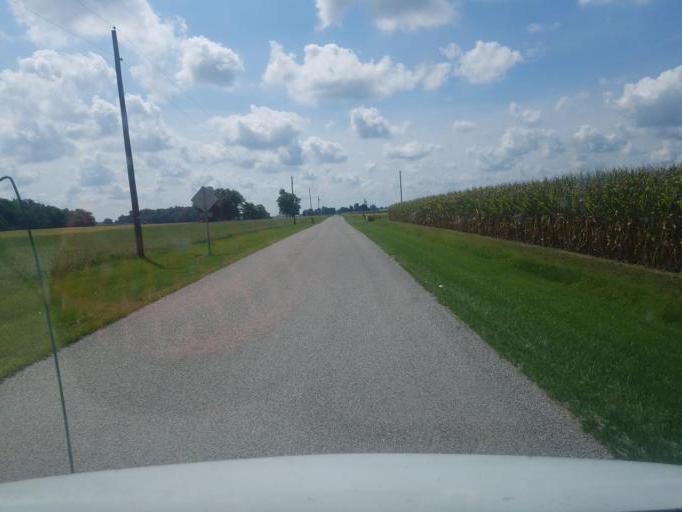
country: US
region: Ohio
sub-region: Marion County
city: Prospect
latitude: 40.4714
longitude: -83.1334
